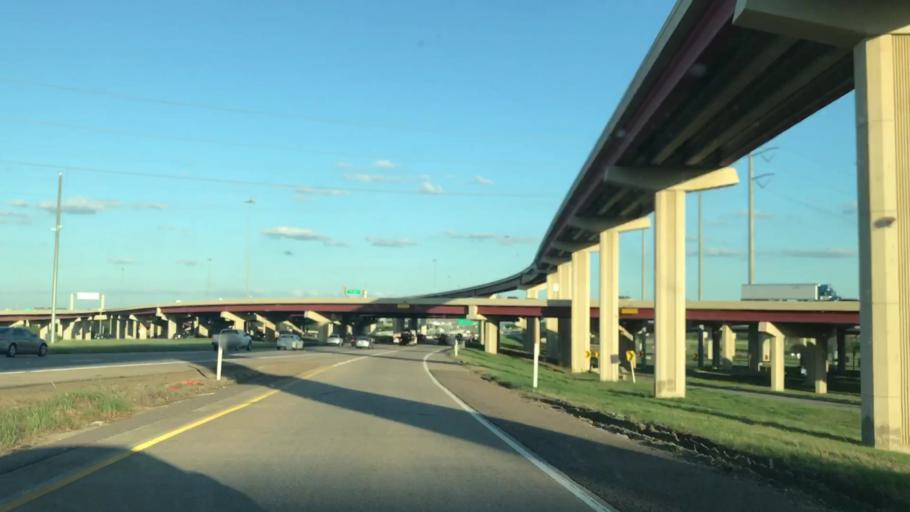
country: US
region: Texas
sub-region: Dallas County
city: Farmers Branch
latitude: 32.9123
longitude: -96.9468
